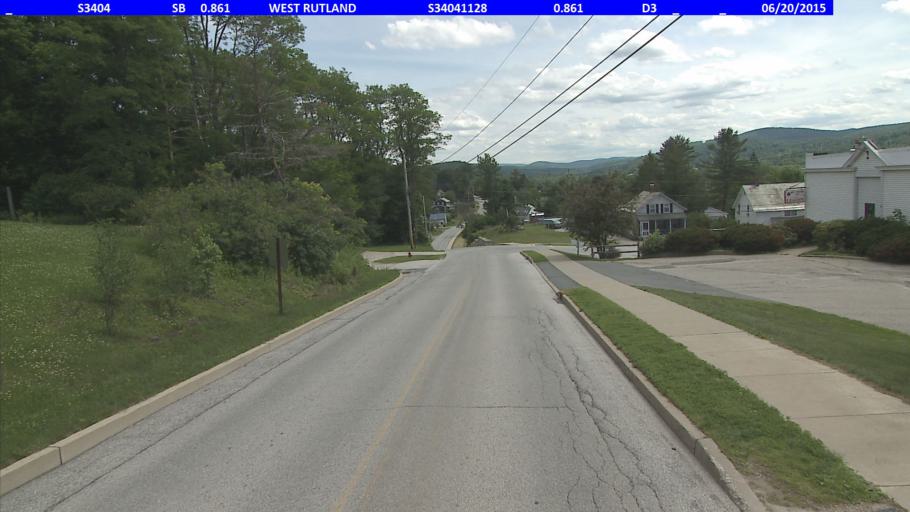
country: US
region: Vermont
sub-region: Rutland County
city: West Rutland
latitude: 43.6042
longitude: -73.0470
